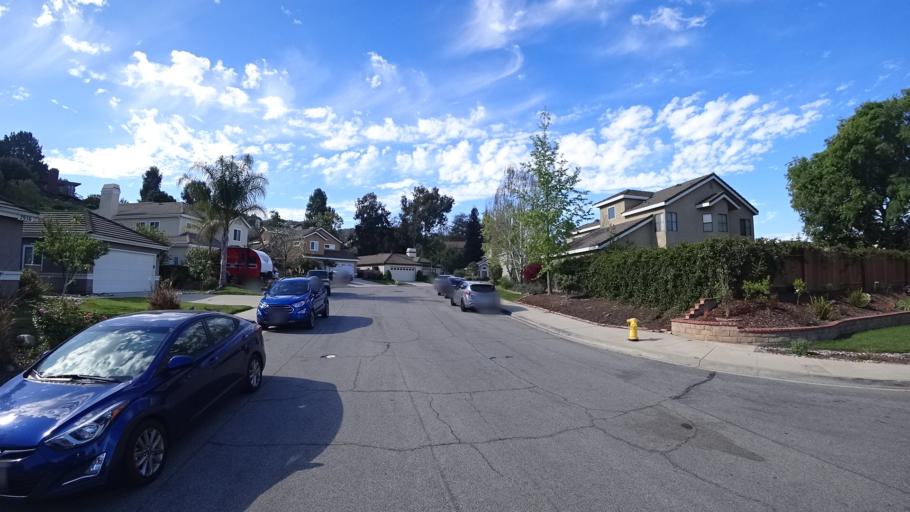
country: US
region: California
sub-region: Ventura County
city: Casa Conejo
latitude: 34.1740
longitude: -118.9392
